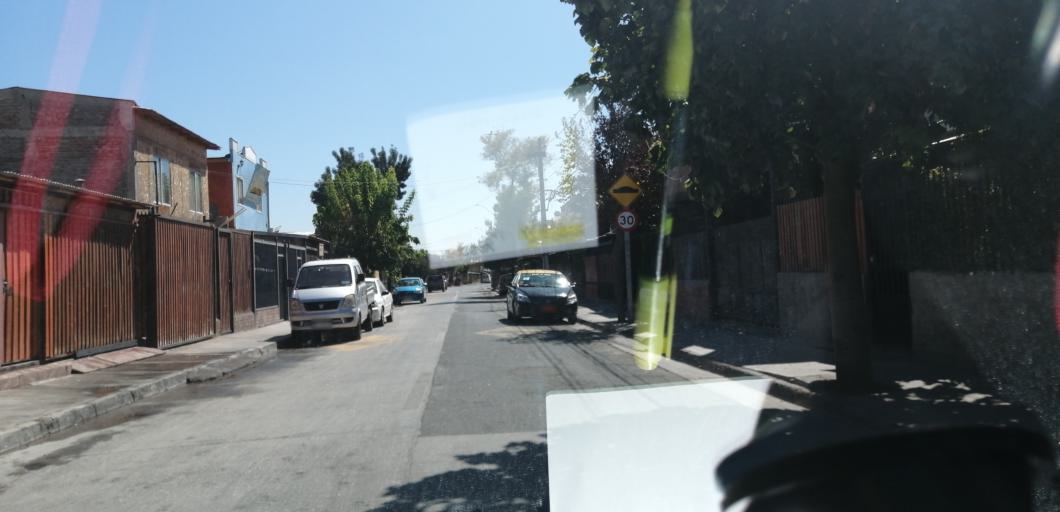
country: CL
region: Santiago Metropolitan
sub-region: Provincia de Santiago
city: Lo Prado
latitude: -33.4405
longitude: -70.7658
